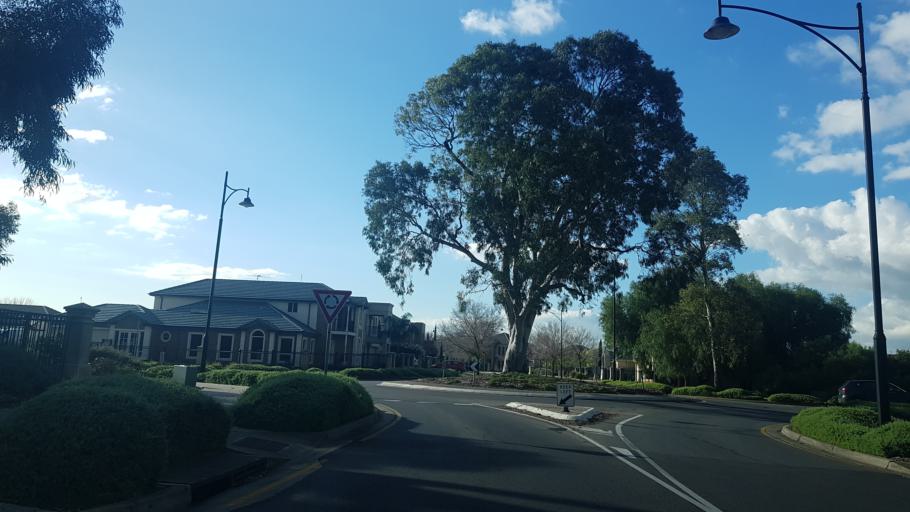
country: AU
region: South Australia
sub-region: Salisbury
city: Ingle Farm
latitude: -34.8194
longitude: 138.6114
